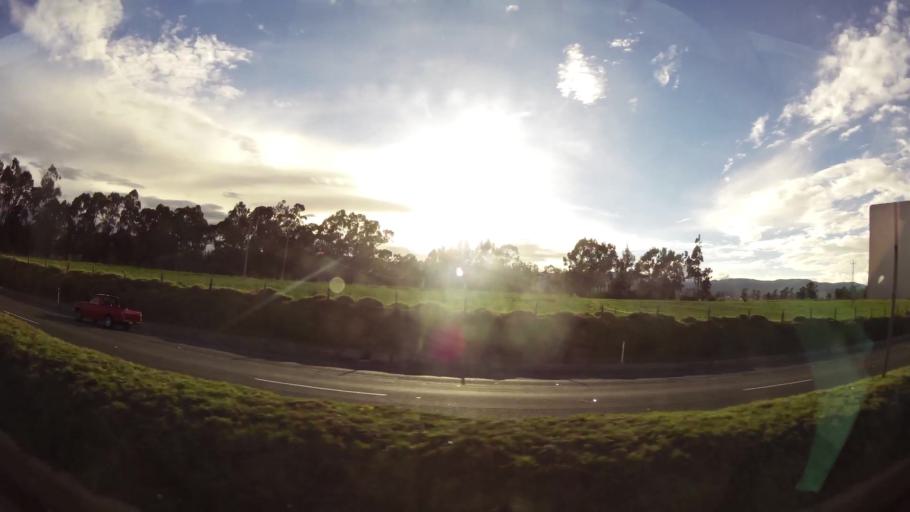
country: EC
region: Cotopaxi
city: Saquisili
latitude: -0.8300
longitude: -78.6191
